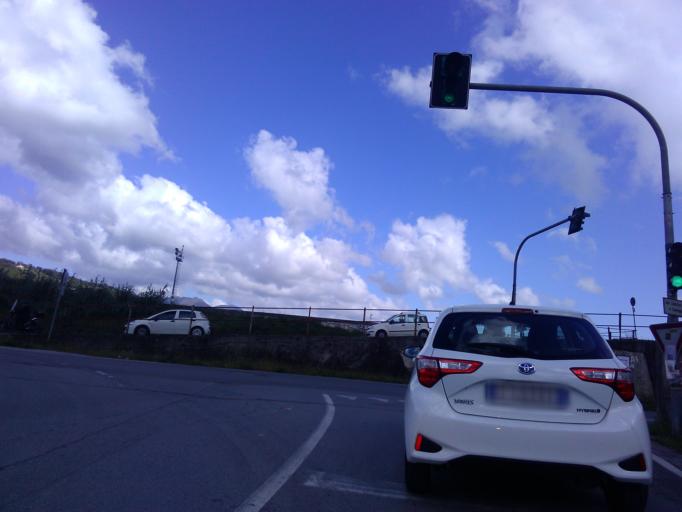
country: IT
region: Tuscany
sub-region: Provincia di Massa-Carrara
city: Capanne-Prato-Cinquale
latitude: 44.0013
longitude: 10.1575
